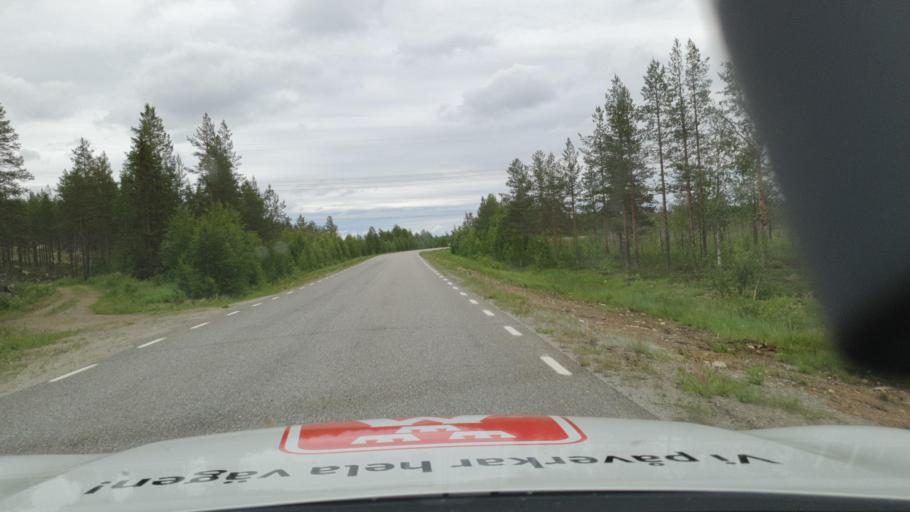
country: SE
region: Vaesterbotten
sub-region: Lycksele Kommun
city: Lycksele
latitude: 64.1658
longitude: 18.3552
